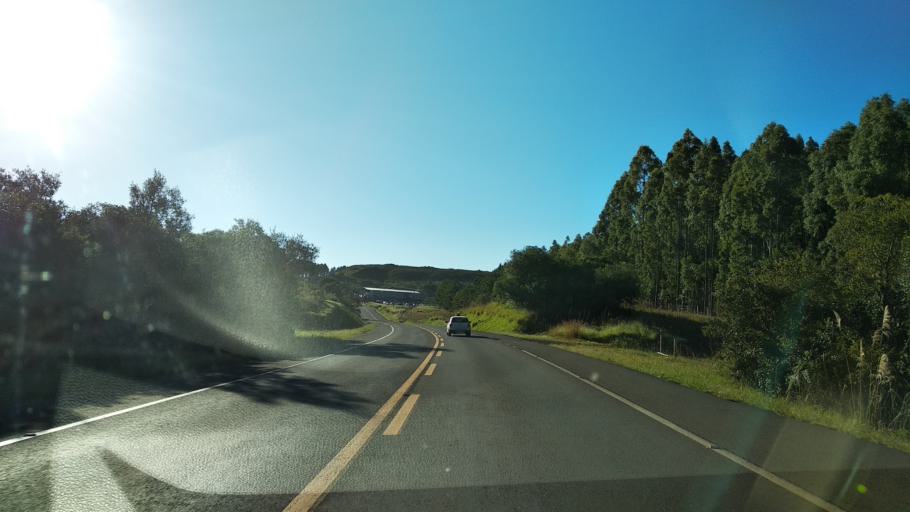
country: BR
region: Santa Catarina
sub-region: Lages
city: Lages
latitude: -27.7880
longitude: -50.4338
